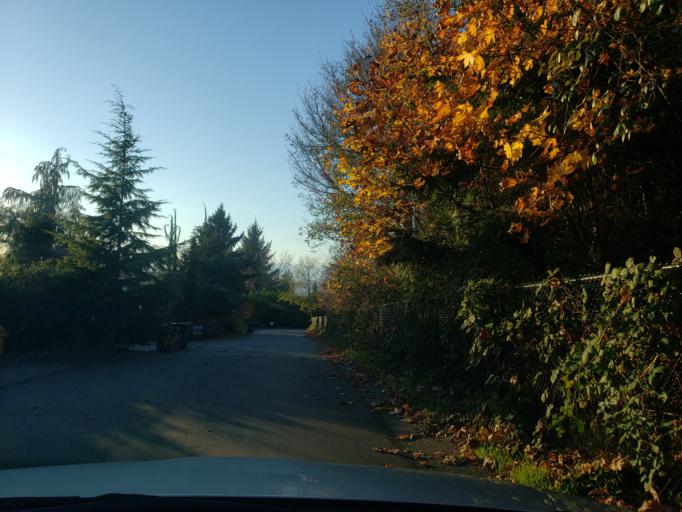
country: US
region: Washington
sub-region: Snohomish County
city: Woodway
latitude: 47.7798
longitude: -122.3843
